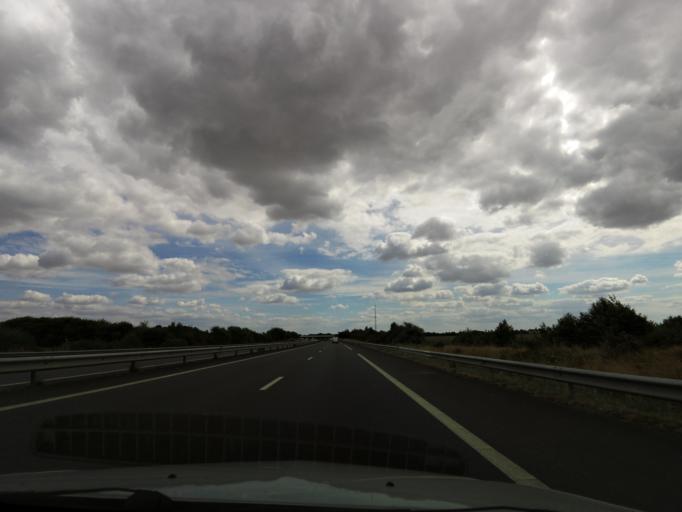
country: FR
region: Pays de la Loire
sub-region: Departement de la Loire-Atlantique
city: La Planche
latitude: 47.0336
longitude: -1.4075
